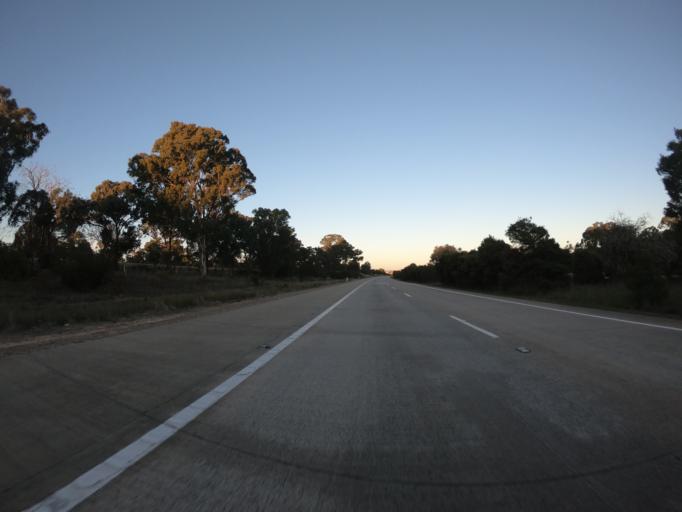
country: AU
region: New South Wales
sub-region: Goulburn Mulwaree
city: Goulburn
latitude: -34.7751
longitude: 149.7509
